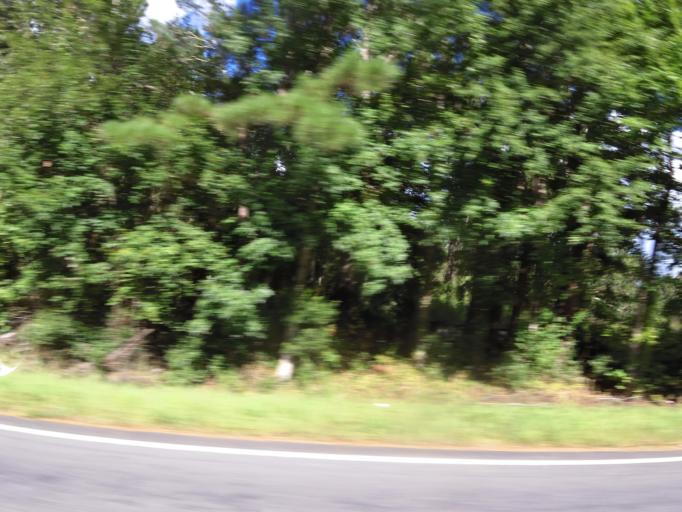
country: US
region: Georgia
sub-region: Camden County
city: Kingsland
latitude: 30.8495
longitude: -81.7001
